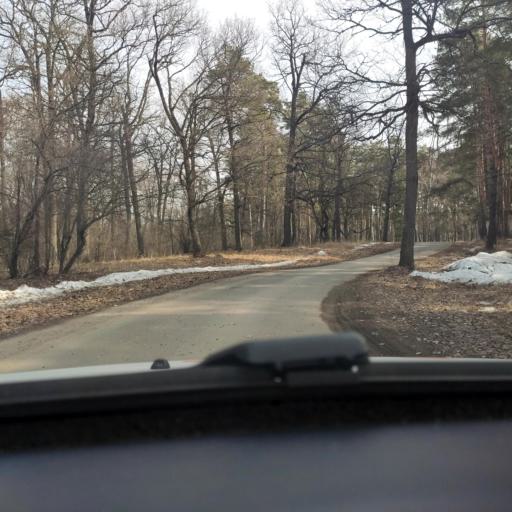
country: RU
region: Voronezj
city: Ramon'
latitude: 51.8909
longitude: 39.3634
